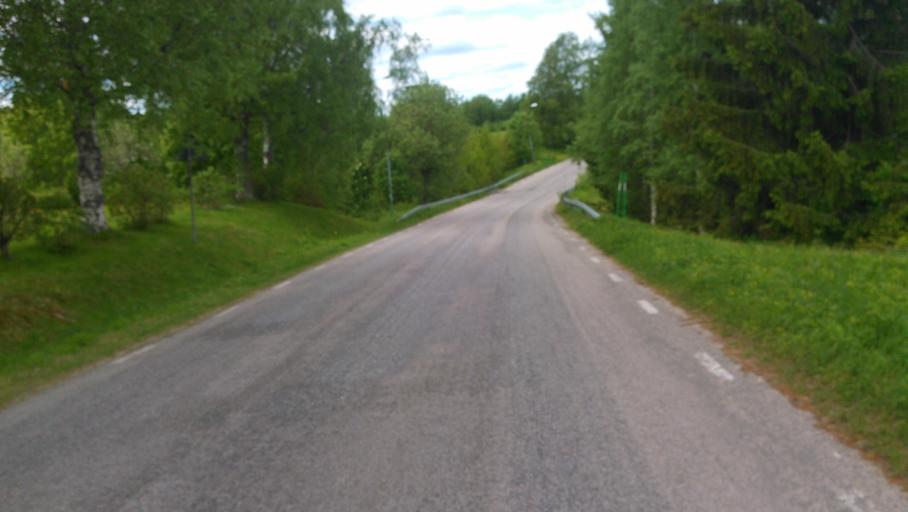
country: SE
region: Vaesterbotten
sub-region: Umea Kommun
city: Roback
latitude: 63.8693
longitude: 20.0683
